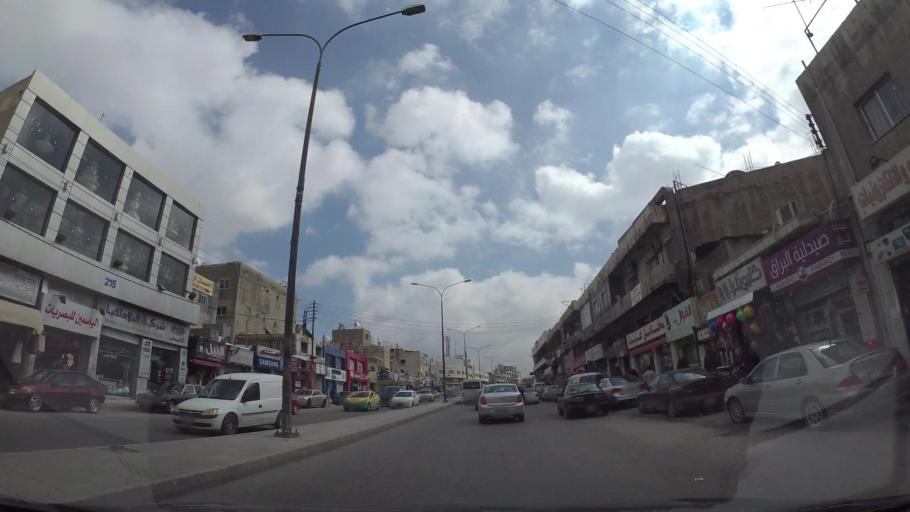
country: JO
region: Amman
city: Al Quwaysimah
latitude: 31.9298
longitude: 35.9364
